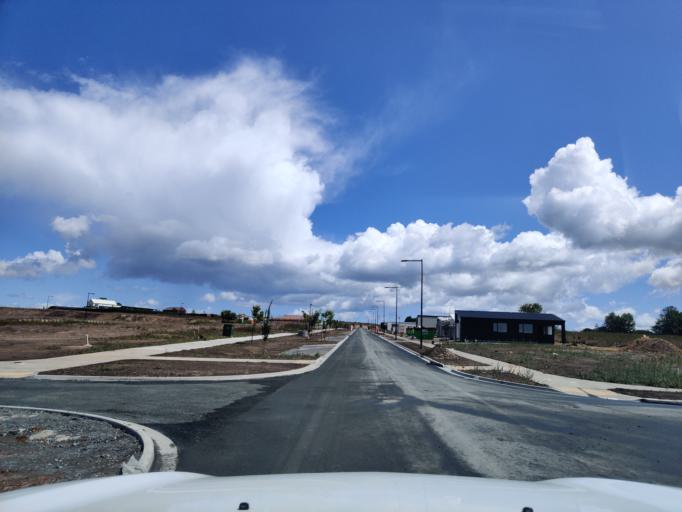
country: NZ
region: Waikato
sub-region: Waikato District
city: Te Kauwhata
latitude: -37.4120
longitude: 175.1519
